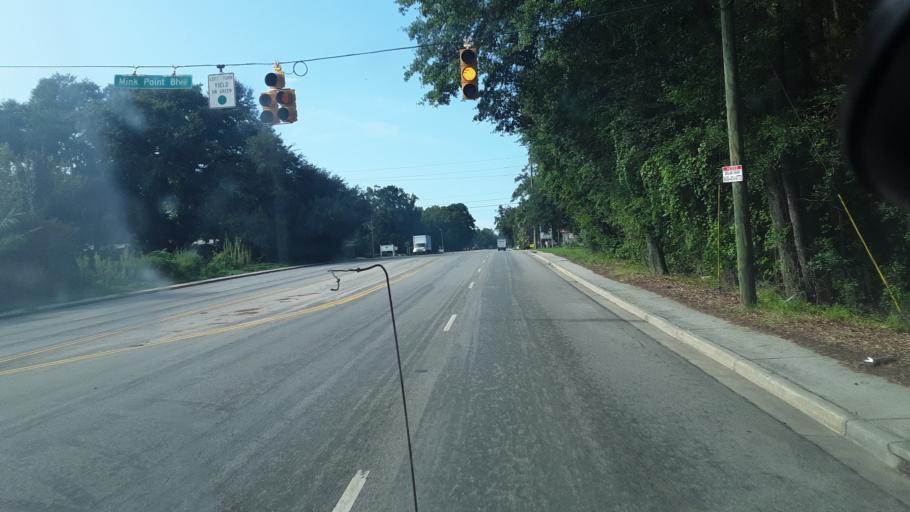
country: US
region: South Carolina
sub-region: Beaufort County
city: Shell Point
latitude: 32.4088
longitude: -80.7335
